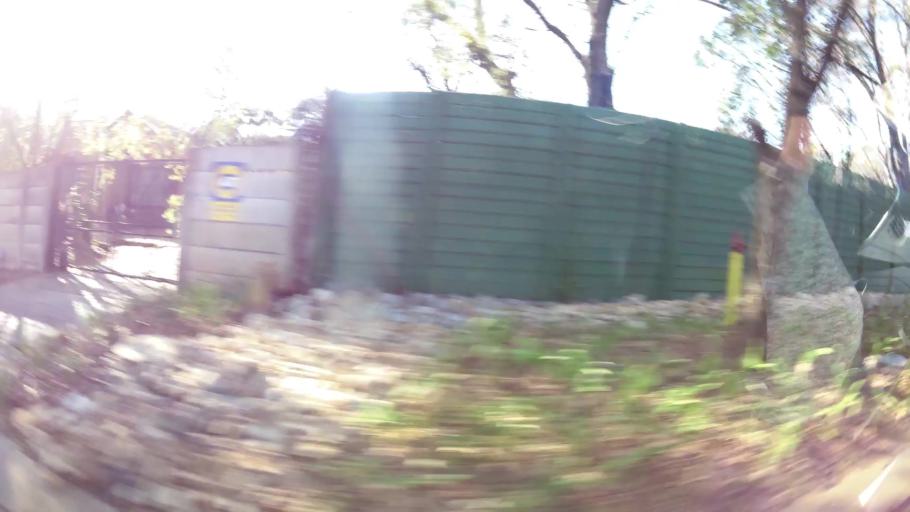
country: ZA
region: Gauteng
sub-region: City of Johannesburg Metropolitan Municipality
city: Midrand
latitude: -26.0712
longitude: 28.0387
